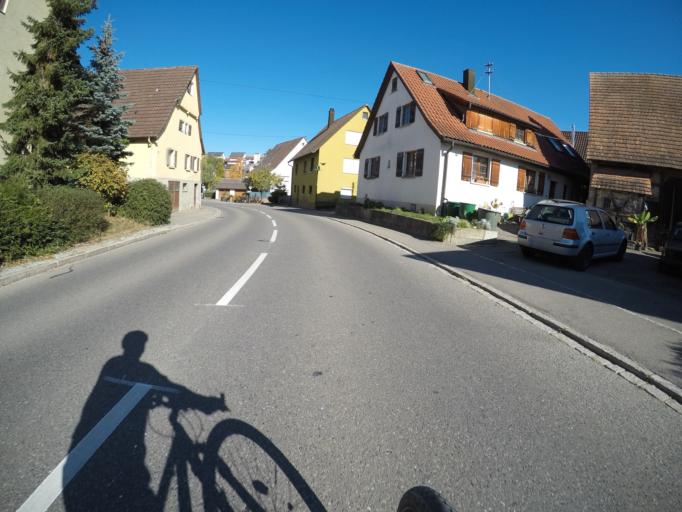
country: DE
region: Baden-Wuerttemberg
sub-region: Tuebingen Region
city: Rottenburg
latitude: 48.5331
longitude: 8.9479
